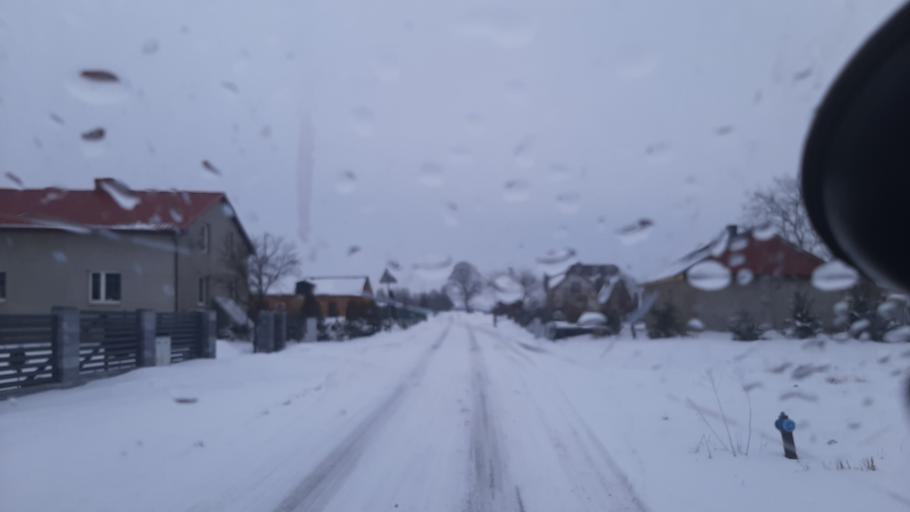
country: PL
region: Lublin Voivodeship
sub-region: Powiat lubelski
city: Garbow
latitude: 51.3567
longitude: 22.3834
